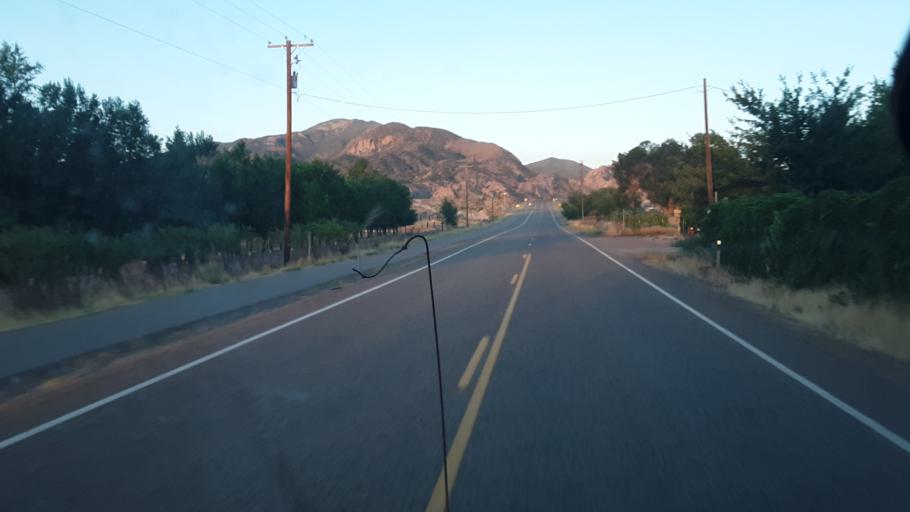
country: US
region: Utah
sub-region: Sevier County
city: Monroe
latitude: 38.5927
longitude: -112.2529
